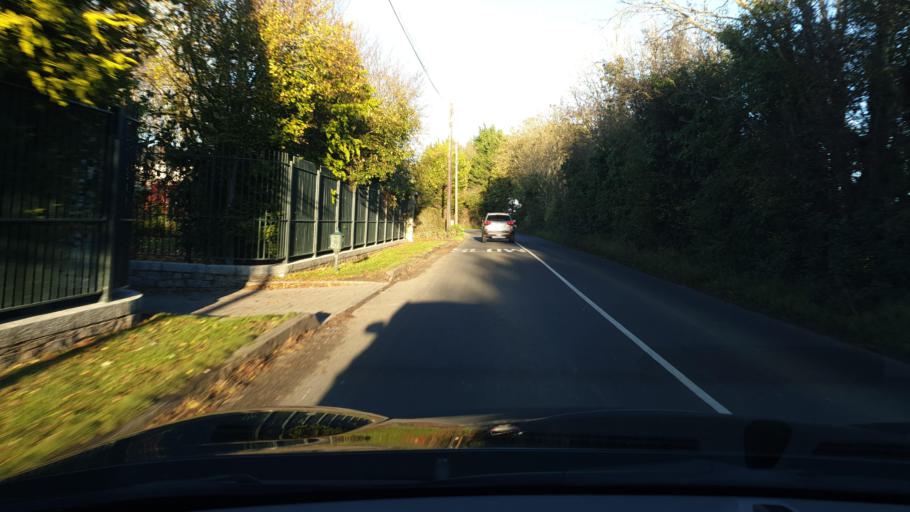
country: IE
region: Leinster
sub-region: Lu
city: Drogheda
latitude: 53.6984
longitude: -6.3131
